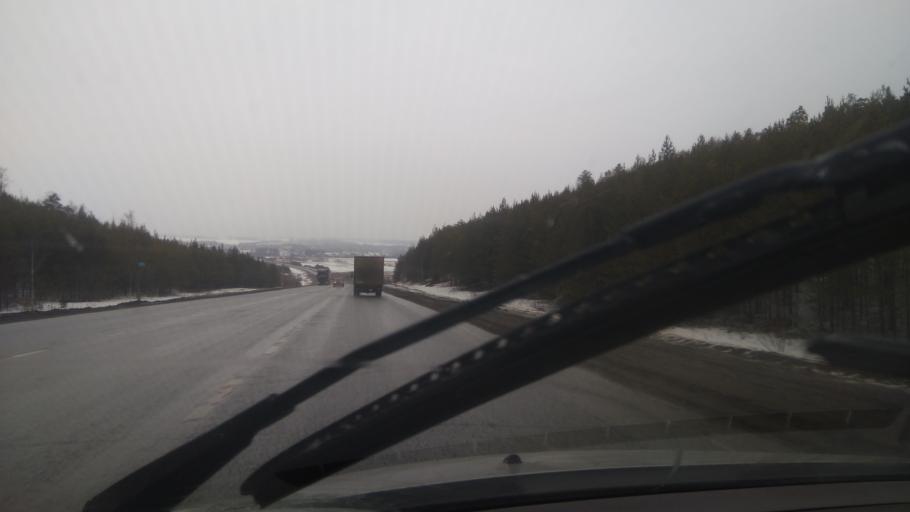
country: RU
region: Perm
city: Kungur
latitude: 57.3525
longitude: 56.9355
